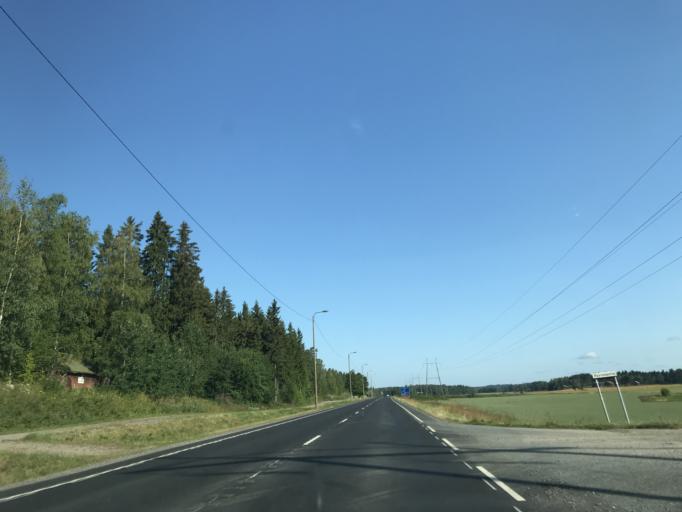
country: FI
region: Paijanne Tavastia
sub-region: Lahti
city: Lahti
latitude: 61.0867
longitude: 25.6530
